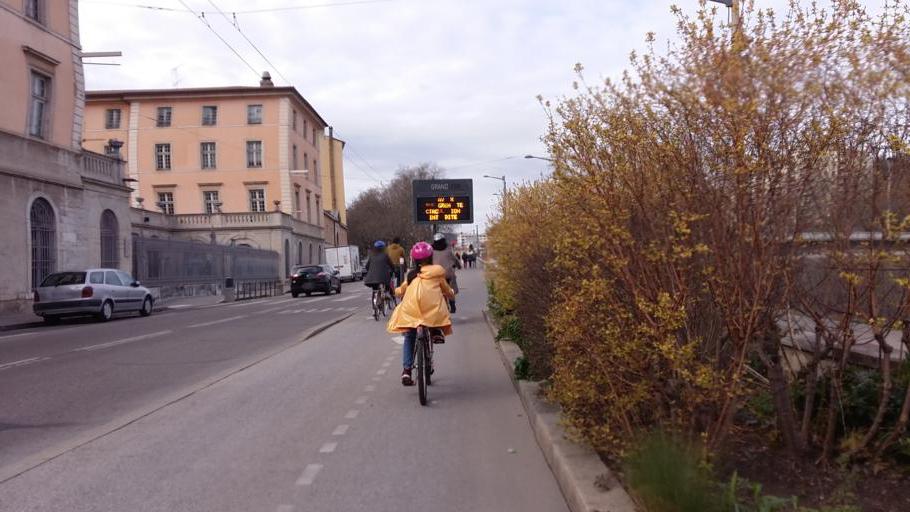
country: FR
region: Rhone-Alpes
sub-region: Departement du Rhone
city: Tassin-la-Demi-Lune
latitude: 45.7687
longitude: 4.8128
